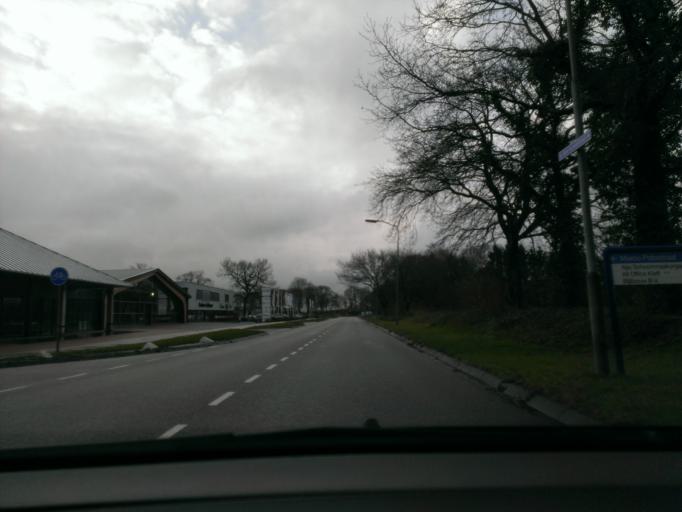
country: NL
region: Drenthe
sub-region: Gemeente Emmen
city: Emmen
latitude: 52.7539
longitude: 6.9154
